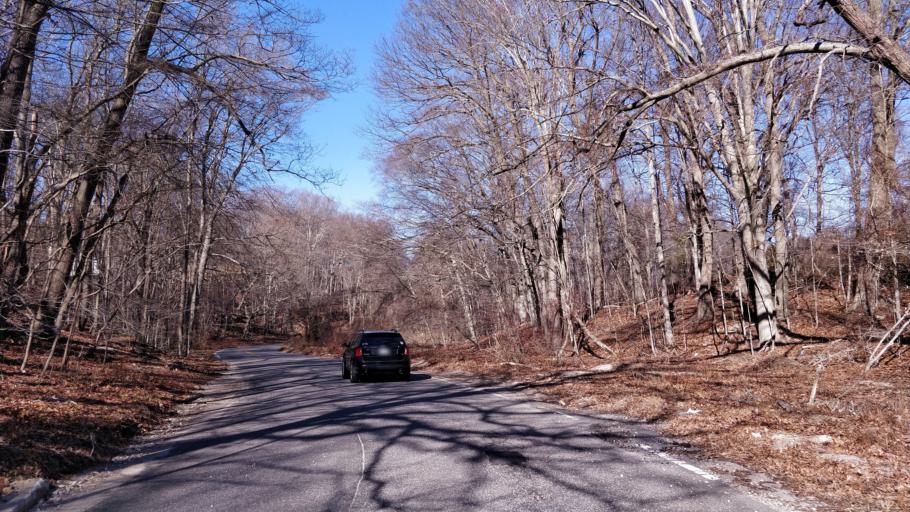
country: US
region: New York
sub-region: Suffolk County
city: Mount Sinai
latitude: 40.9495
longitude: -73.0422
